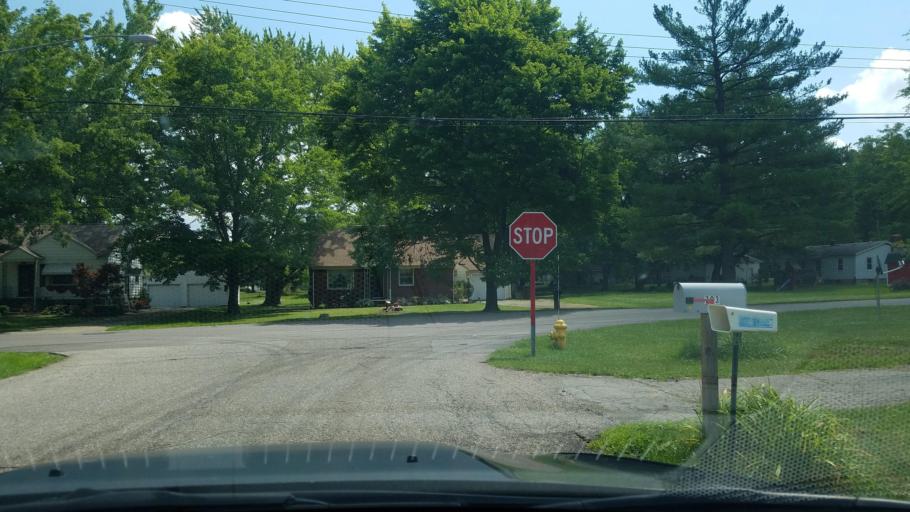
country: US
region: Ohio
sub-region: Trumbull County
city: Champion Heights
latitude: 41.2917
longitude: -80.8613
